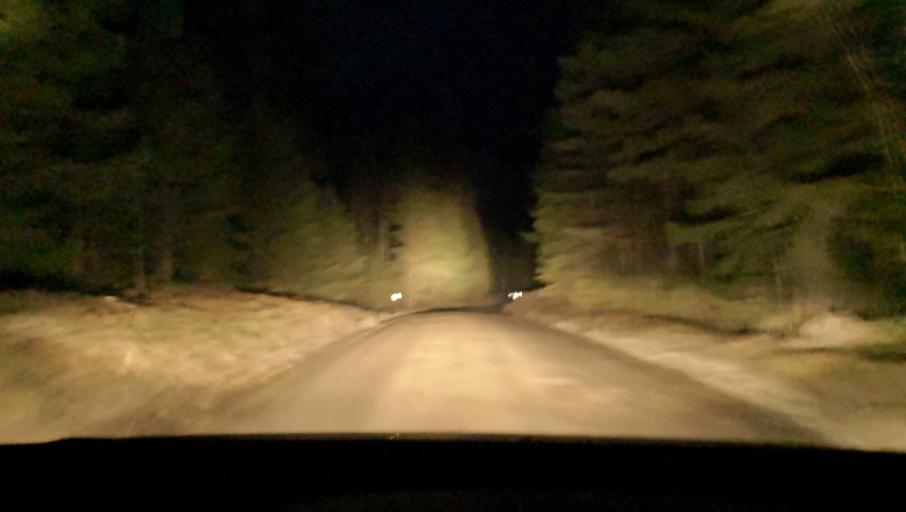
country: SE
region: Vaestmanland
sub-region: Skinnskattebergs Kommun
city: Skinnskatteberg
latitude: 59.6691
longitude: 15.5758
